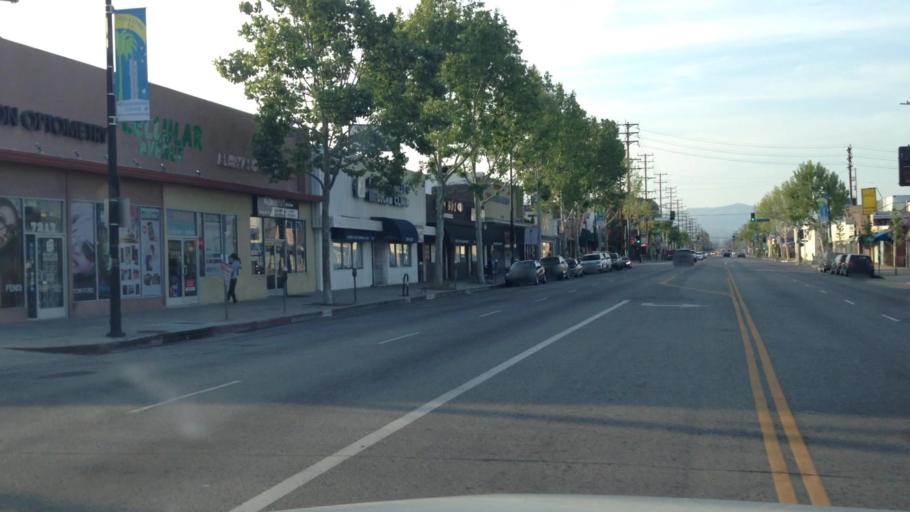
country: US
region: California
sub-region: Los Angeles County
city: Northridge
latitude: 34.2015
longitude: -118.5361
